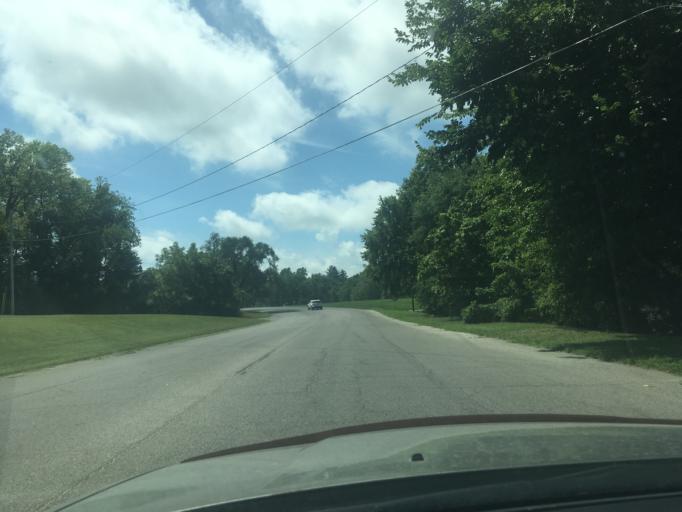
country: US
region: Kansas
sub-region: Atchison County
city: Atchison
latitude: 39.5506
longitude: -95.1197
